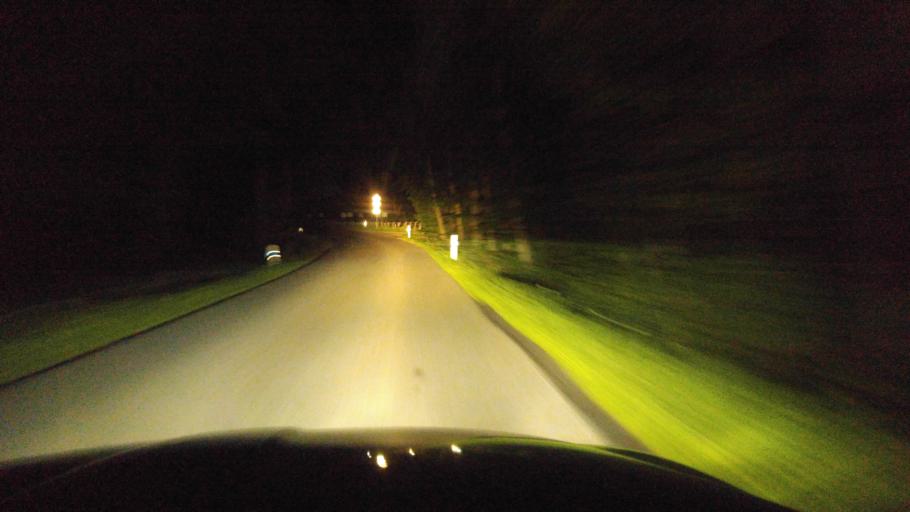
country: DE
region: North Rhine-Westphalia
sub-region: Regierungsbezirk Koln
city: Numbrecht
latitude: 50.8901
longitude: 7.5519
